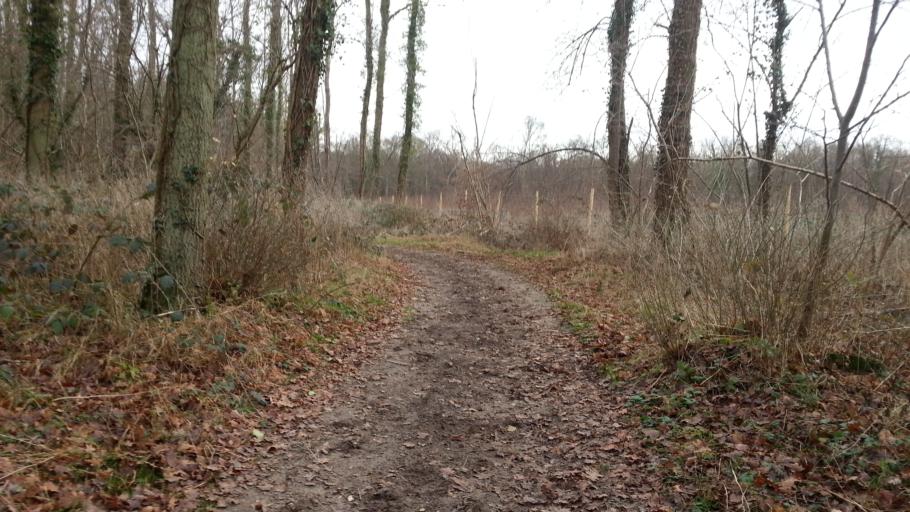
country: FR
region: Picardie
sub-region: Departement de l'Oise
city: Gouvieux
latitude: 49.1859
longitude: 2.3923
